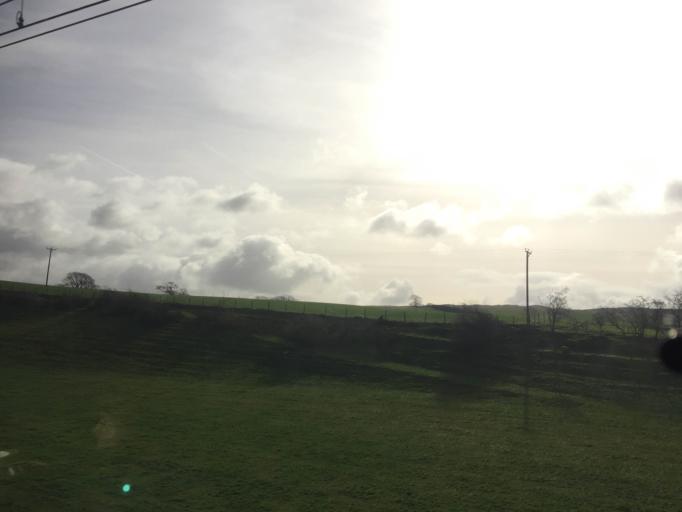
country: GB
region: England
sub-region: Cumbria
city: Kendal
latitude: 54.3568
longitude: -2.6610
